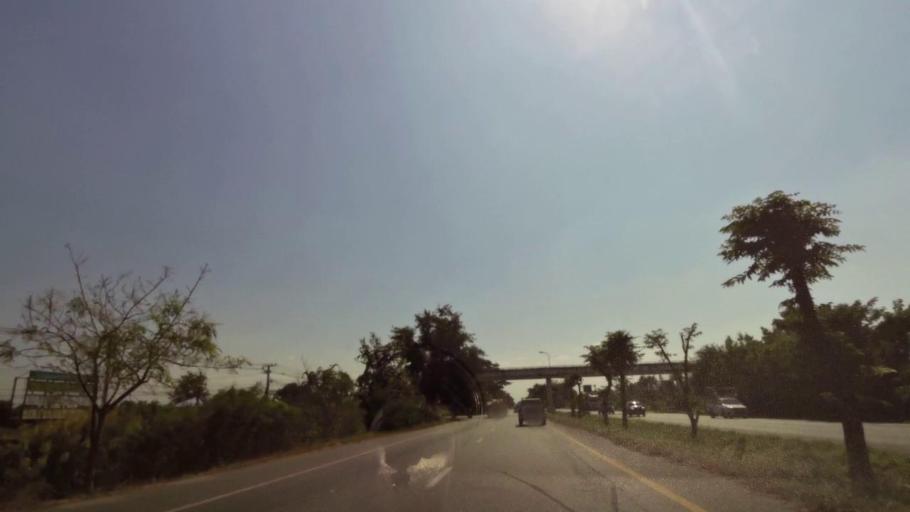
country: TH
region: Nakhon Sawan
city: Kao Liao
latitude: 15.7947
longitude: 100.1207
